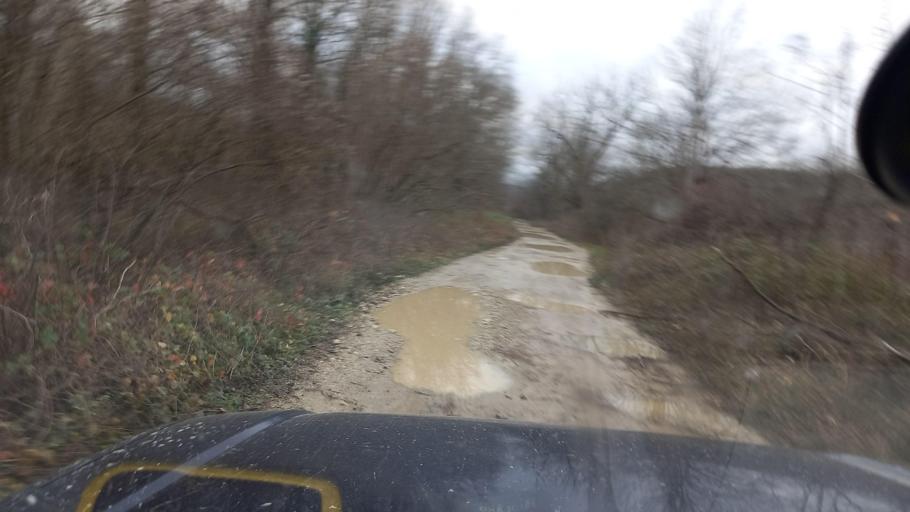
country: RU
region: Krasnodarskiy
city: Pshada
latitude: 44.4897
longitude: 38.4110
